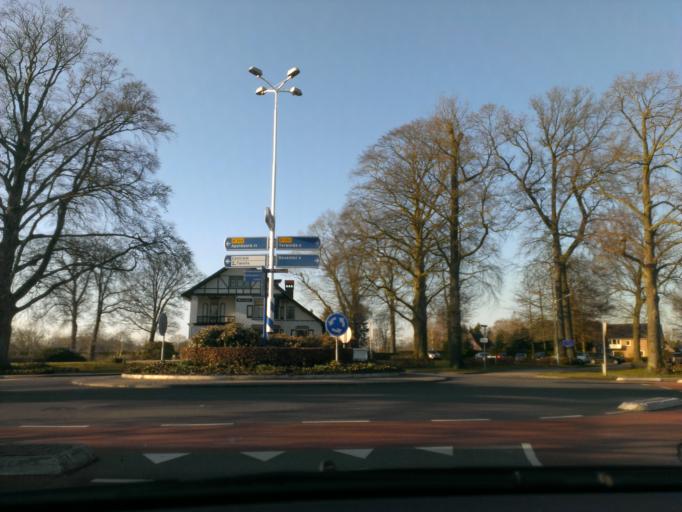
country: NL
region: Gelderland
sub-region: Gemeente Voorst
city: Twello
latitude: 52.2414
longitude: 6.1049
